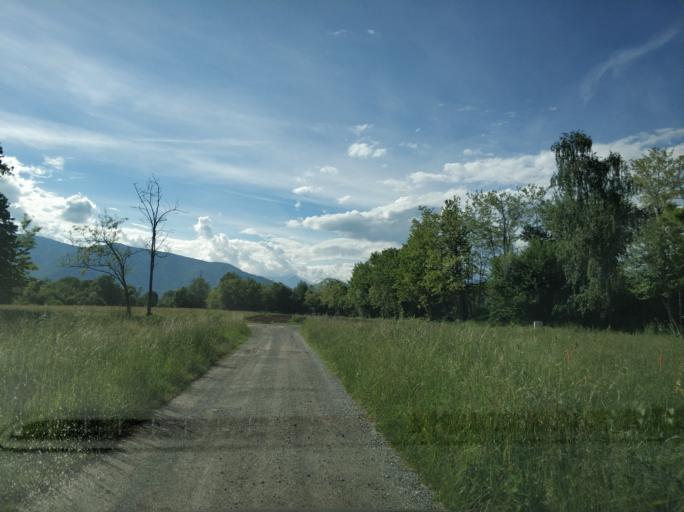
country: IT
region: Piedmont
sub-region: Provincia di Torino
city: Nole
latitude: 45.2285
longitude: 7.5737
